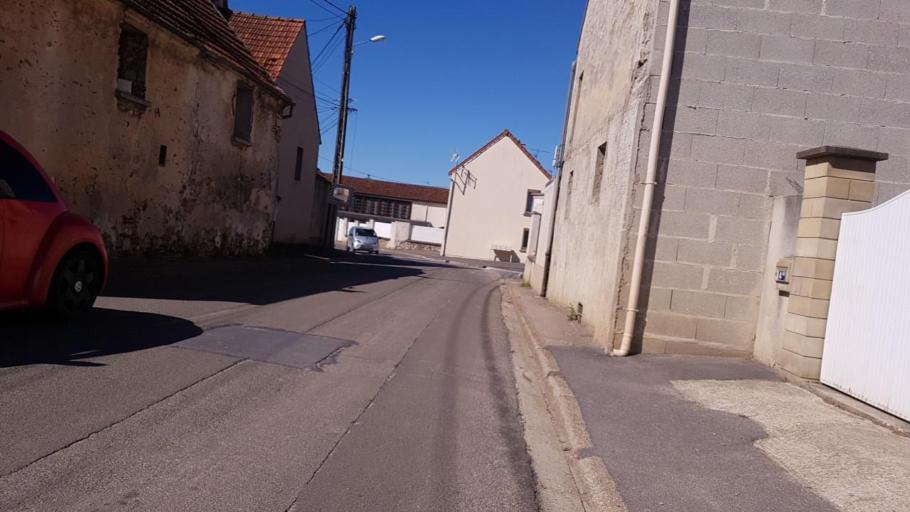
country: FR
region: Picardie
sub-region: Departement de l'Aisne
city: Chezy-sur-Marne
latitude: 48.9773
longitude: 3.3375
